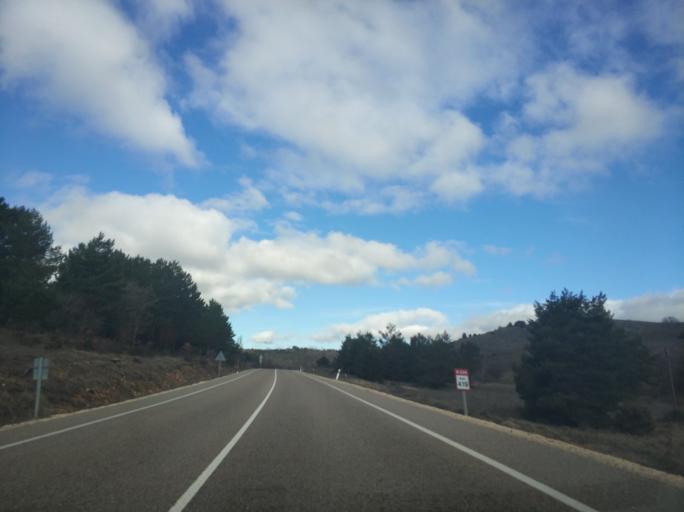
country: ES
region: Castille and Leon
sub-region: Provincia de Burgos
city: Rabanera del Pinar
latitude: 41.8782
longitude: -3.2226
